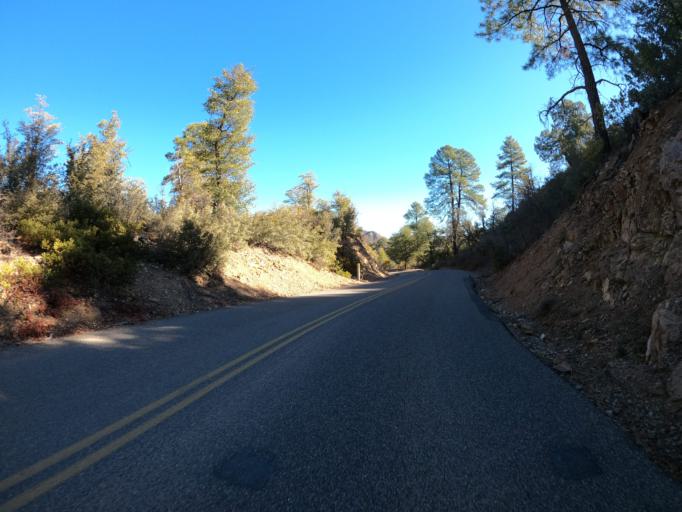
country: US
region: Arizona
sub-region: Yavapai County
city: Verde Village
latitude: 34.5876
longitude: -112.0558
